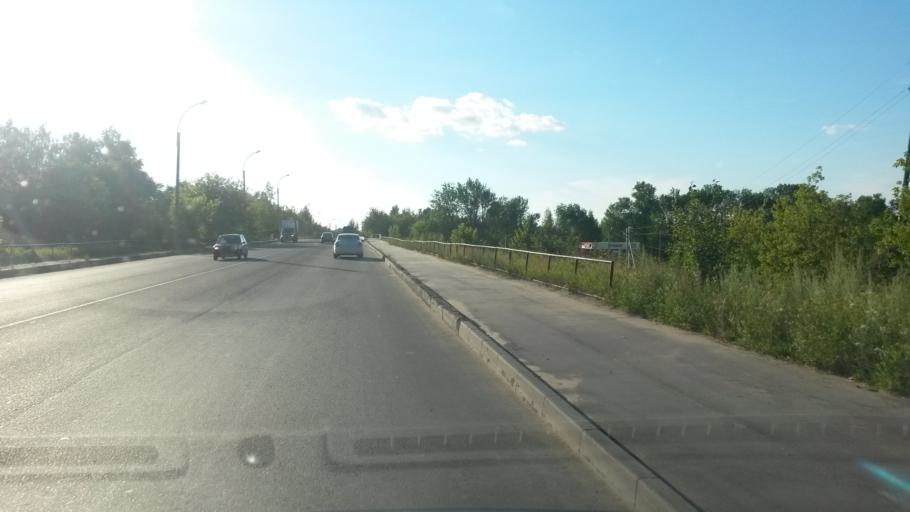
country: RU
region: Ivanovo
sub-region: Gorod Ivanovo
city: Ivanovo
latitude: 57.0164
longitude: 40.9278
